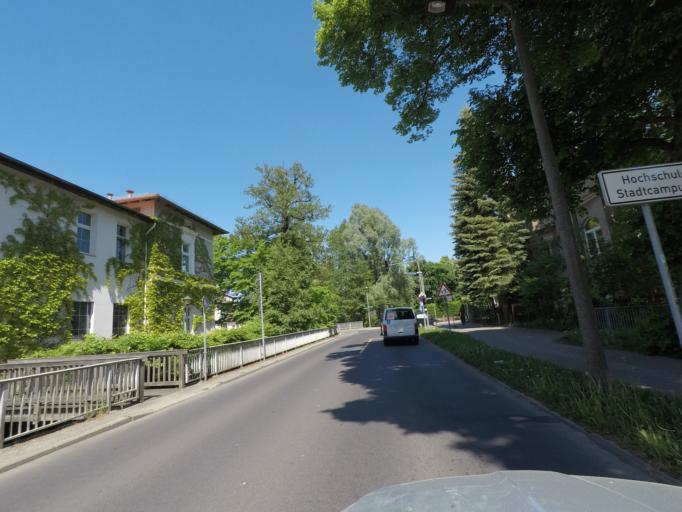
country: DE
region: Brandenburg
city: Eberswalde
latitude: 52.8299
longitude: 13.8122
